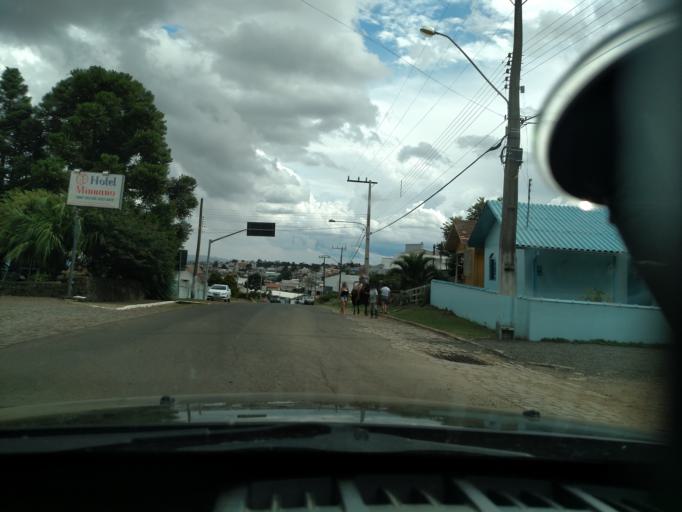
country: BR
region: Santa Catarina
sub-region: Sao Joaquim
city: Sao Joaquim
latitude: -28.2757
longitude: -49.9280
